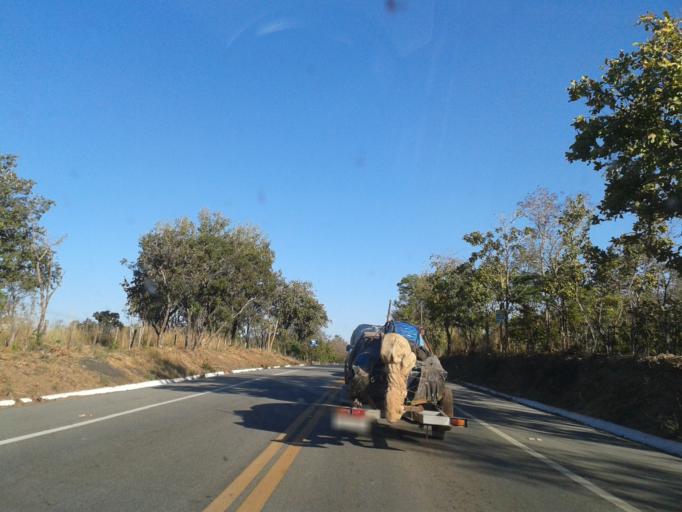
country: BR
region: Goias
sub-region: Itapuranga
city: Itapuranga
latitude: -15.5066
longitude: -50.3031
